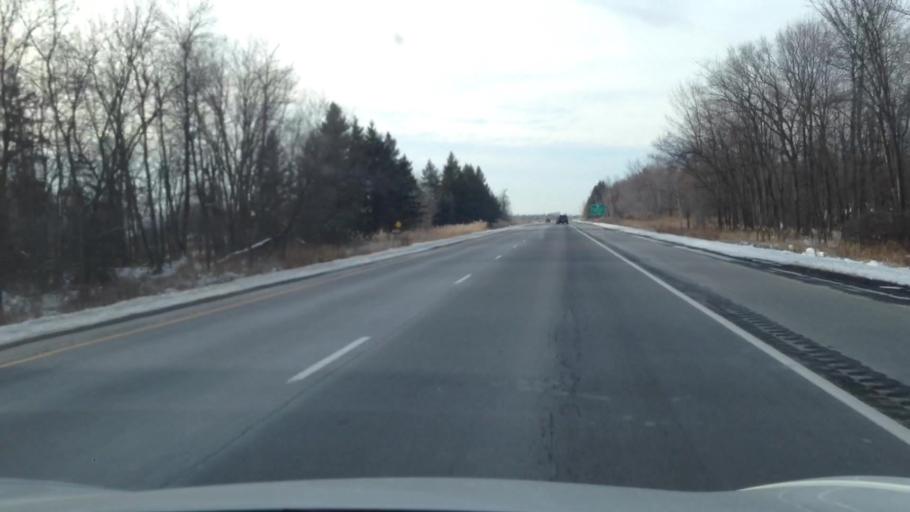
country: CA
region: Quebec
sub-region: Laurentides
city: Brownsburg-Chatham
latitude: 45.5618
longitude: -74.4824
